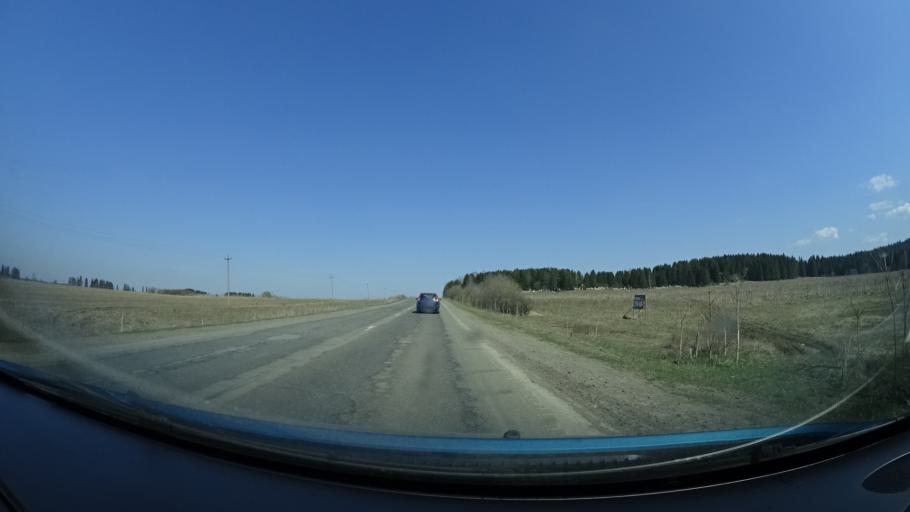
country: RU
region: Perm
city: Kultayevo
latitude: 57.8566
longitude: 55.8606
